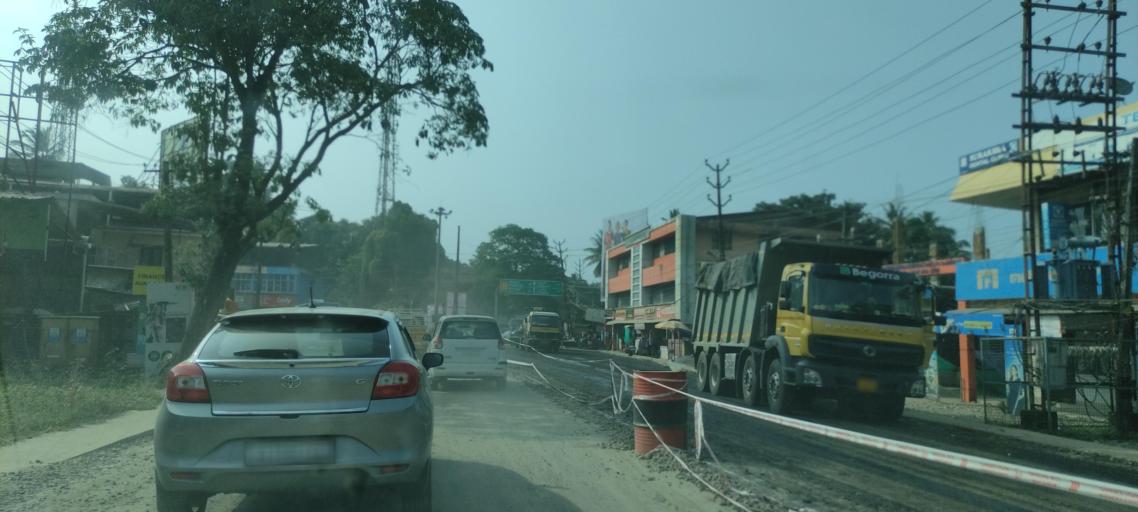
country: IN
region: Kerala
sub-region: Pattanamtitta
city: Tiruvalla
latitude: 9.3663
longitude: 76.5457
